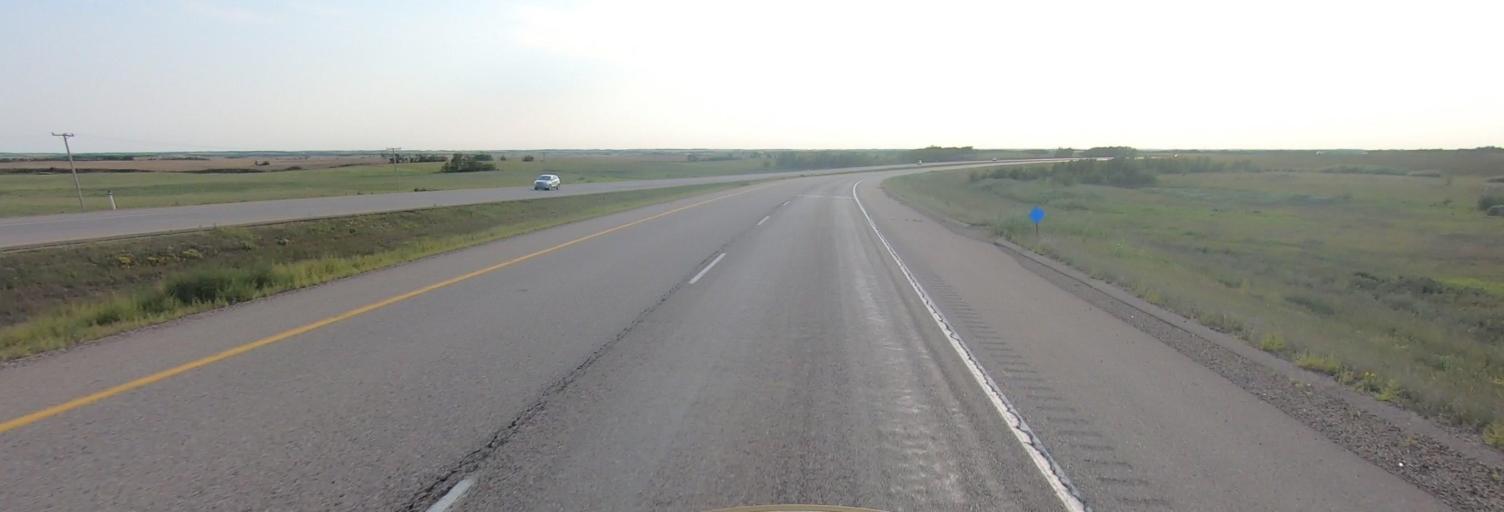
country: CA
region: Saskatchewan
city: Melville
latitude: 50.3796
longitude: -102.6103
